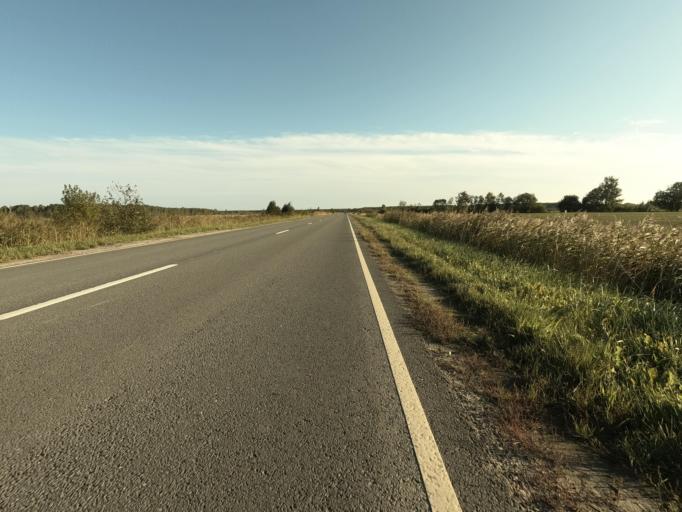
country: RU
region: St.-Petersburg
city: Sapernyy
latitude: 59.7391
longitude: 30.6522
